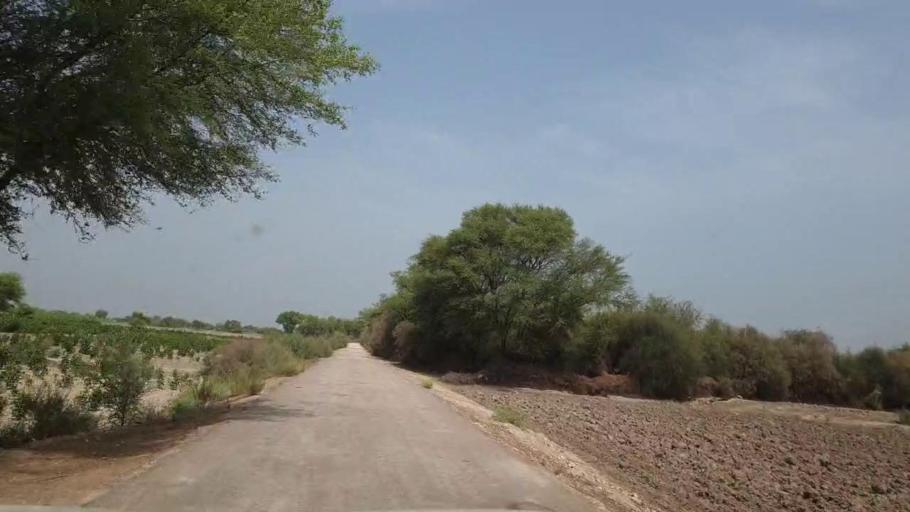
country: PK
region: Sindh
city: Sobhadero
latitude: 27.3952
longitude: 68.2611
